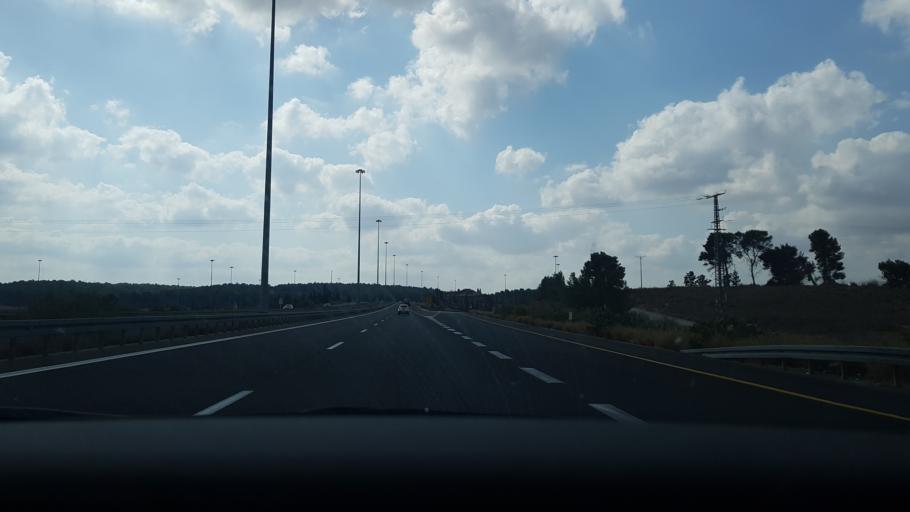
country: IL
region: Southern District
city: Qiryat Gat
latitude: 31.6046
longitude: 34.8132
